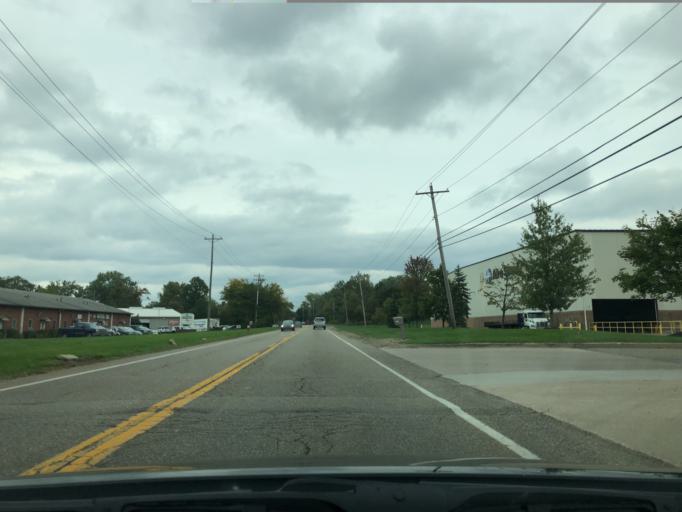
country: US
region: Ohio
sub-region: Summit County
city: Silver Lake
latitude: 41.1991
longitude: -81.4992
